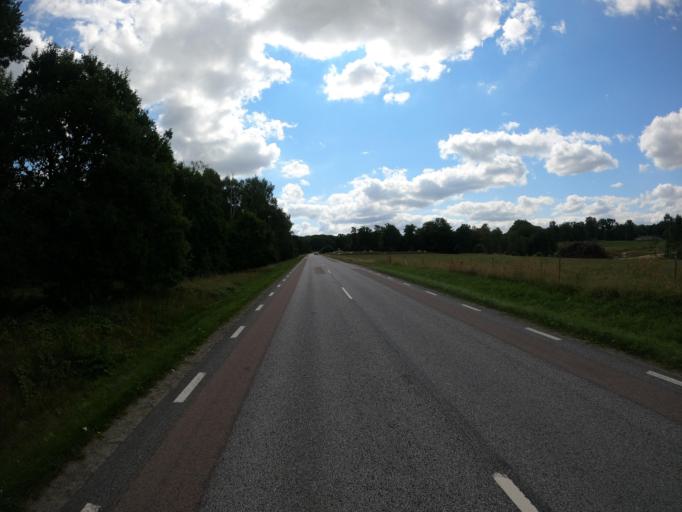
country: SE
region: Skane
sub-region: Lunds Kommun
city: Veberod
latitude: 55.6209
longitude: 13.4929
